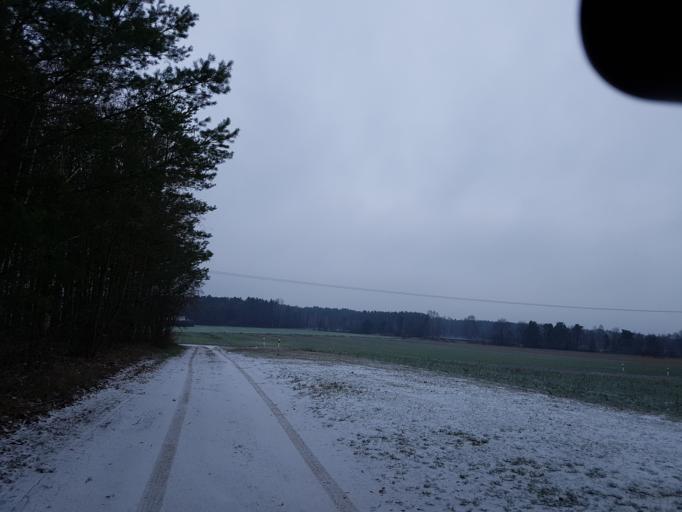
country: DE
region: Brandenburg
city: Schonborn
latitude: 51.5604
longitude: 13.4879
